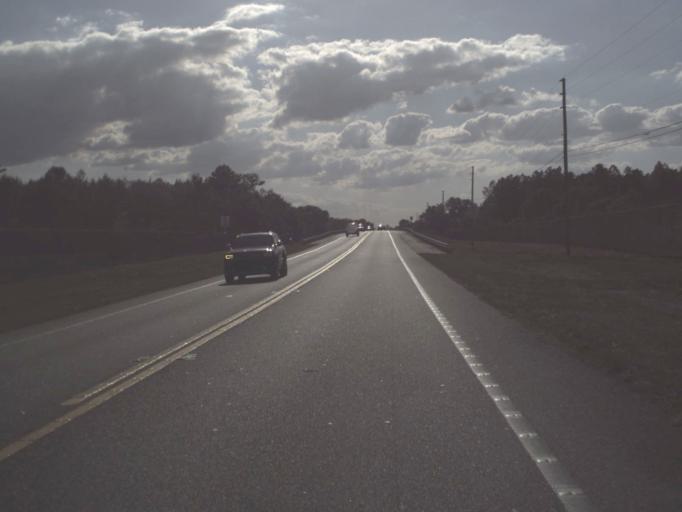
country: US
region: Florida
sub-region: Lake County
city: Mount Plymouth
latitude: 28.8110
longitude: -81.4515
